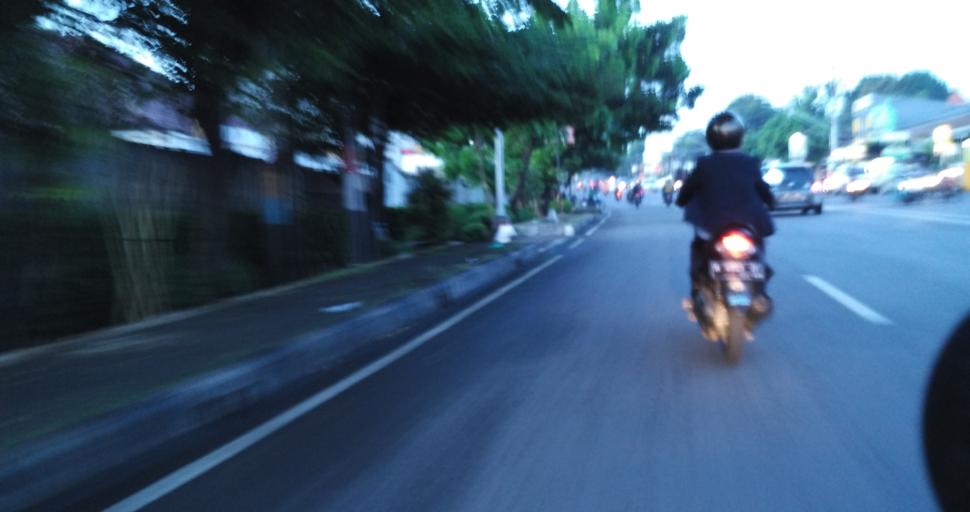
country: ID
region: Central Java
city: Semarang
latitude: -7.0463
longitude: 110.4209
